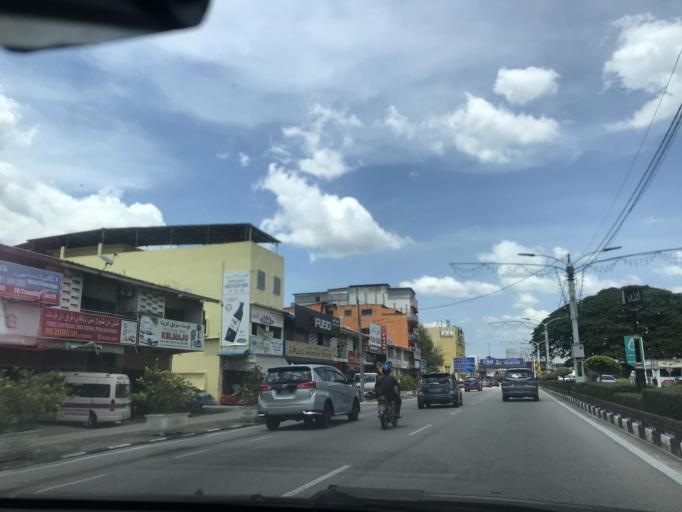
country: MY
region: Kelantan
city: Kota Bharu
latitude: 6.1197
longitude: 102.2410
